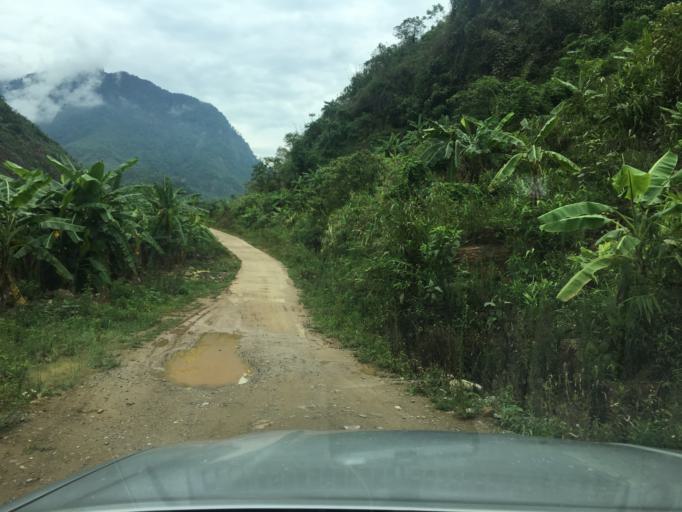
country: VN
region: Yen Bai
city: Son Thinh
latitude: 21.6758
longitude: 104.5374
